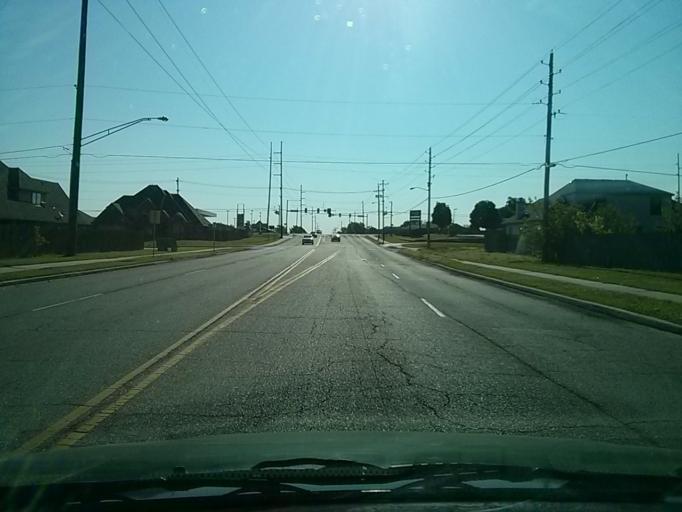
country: US
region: Oklahoma
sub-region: Tulsa County
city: Tulsa
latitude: 36.1770
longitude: -95.9957
